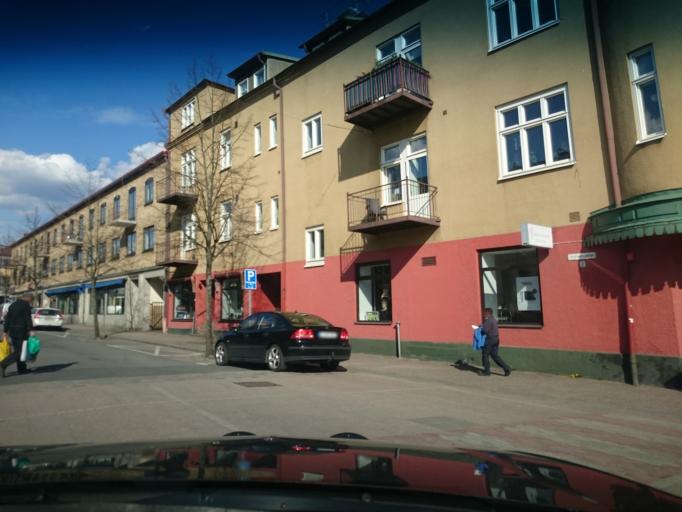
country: SE
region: Joenkoeping
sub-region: Vetlanda Kommun
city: Vetlanda
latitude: 57.4261
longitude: 15.0825
